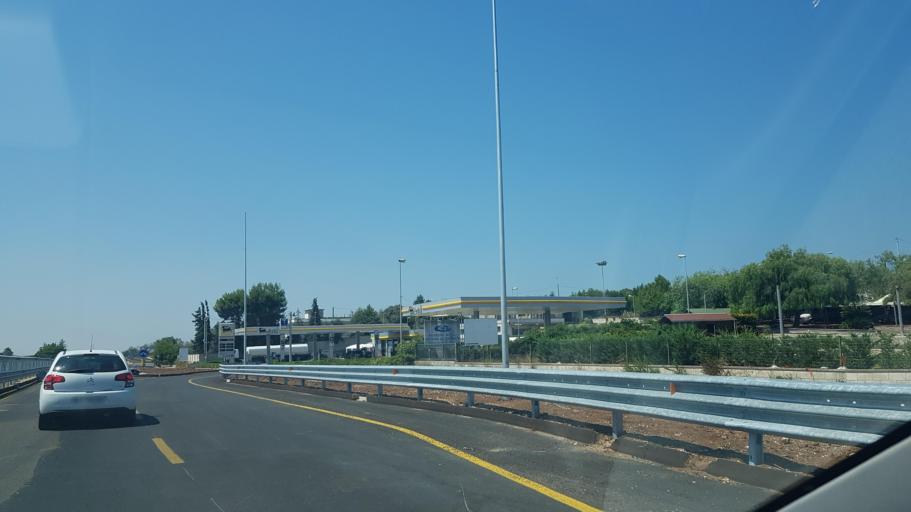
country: IT
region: Apulia
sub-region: Provincia di Lecce
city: Struda
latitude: 40.3158
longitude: 18.2770
